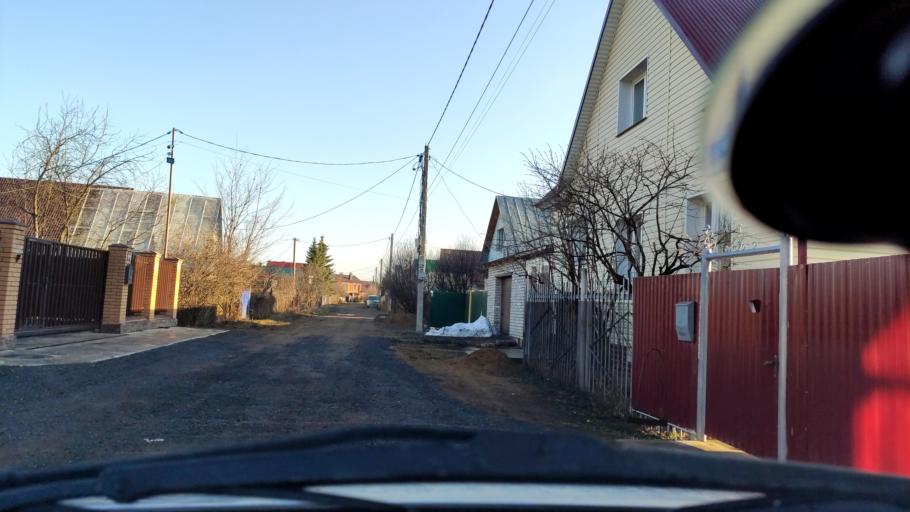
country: RU
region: Bashkortostan
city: Mikhaylovka
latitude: 54.8057
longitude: 55.9412
